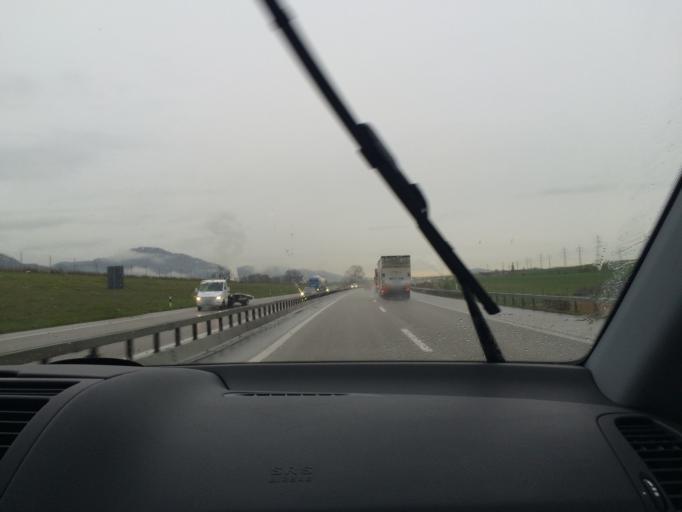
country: CH
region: Bern
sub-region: Oberaargau
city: Oberbipp
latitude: 47.2531
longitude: 7.6743
